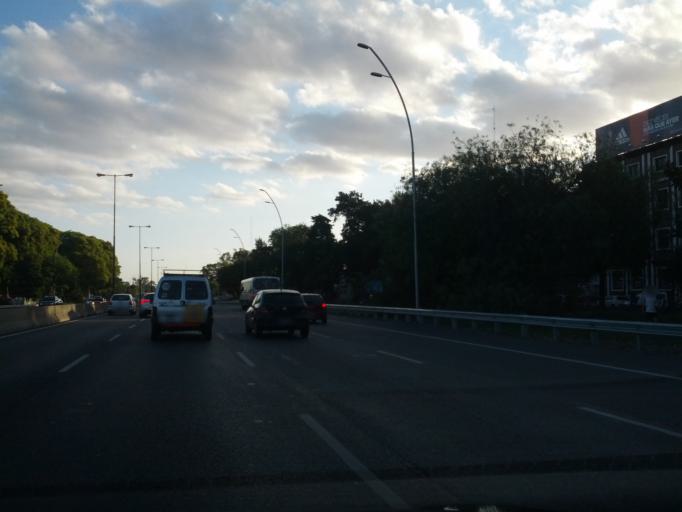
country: AR
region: Buenos Aires
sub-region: Partido de General San Martin
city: General San Martin
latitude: -34.6070
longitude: -58.5269
